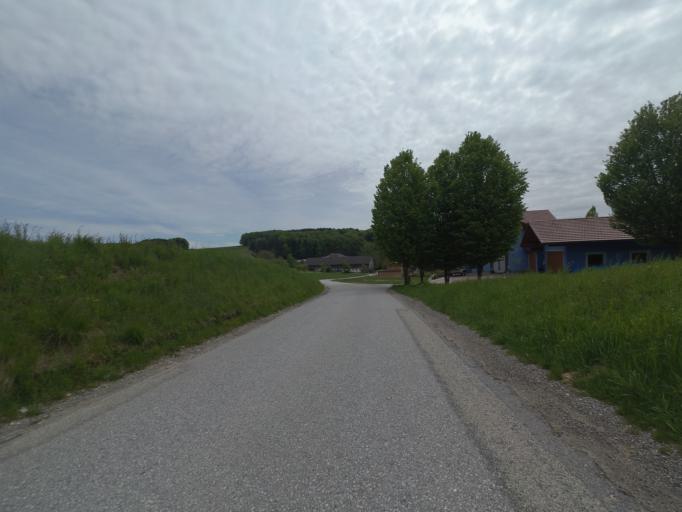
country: AT
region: Salzburg
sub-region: Politischer Bezirk Salzburg-Umgebung
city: Schleedorf
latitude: 47.9990
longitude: 13.1556
